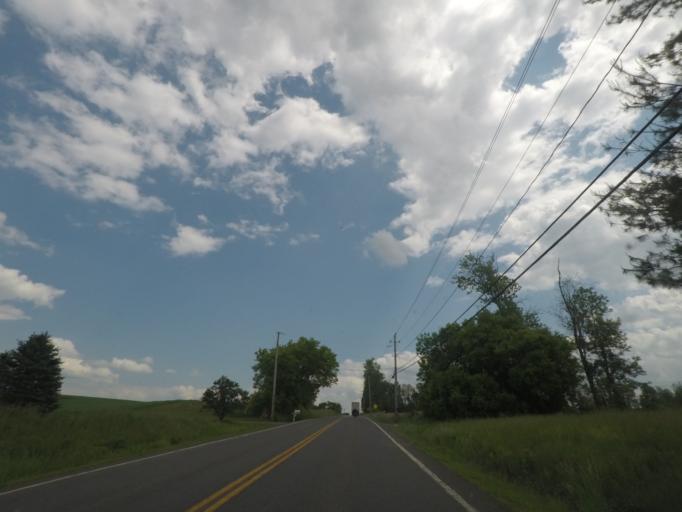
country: US
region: New York
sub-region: Dutchess County
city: Pine Plains
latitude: 42.0478
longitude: -73.6201
